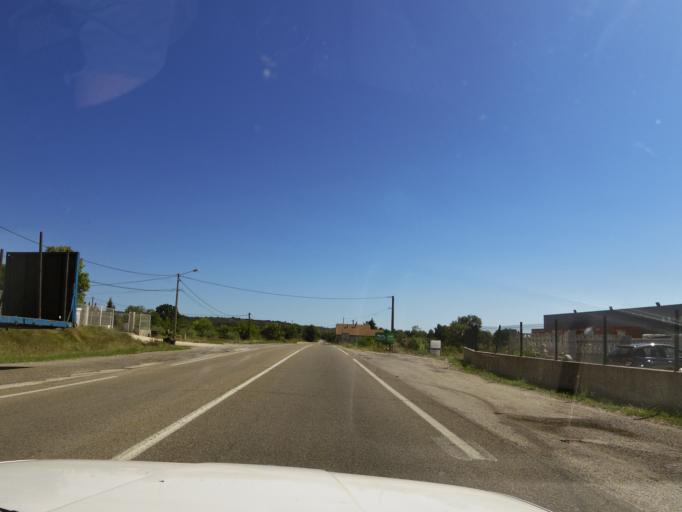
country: FR
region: Languedoc-Roussillon
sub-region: Departement du Gard
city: Saint-Hilaire-de-Brethmas
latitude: 44.0876
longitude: 4.1103
